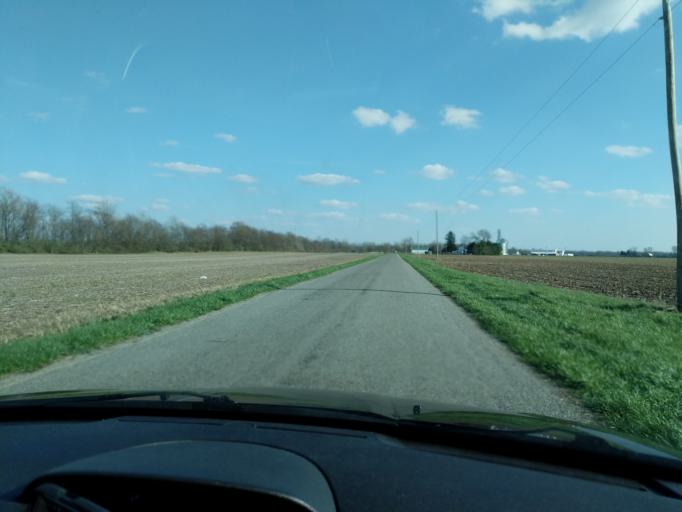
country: US
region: Ohio
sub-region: Champaign County
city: Urbana
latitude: 40.1137
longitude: -83.8046
